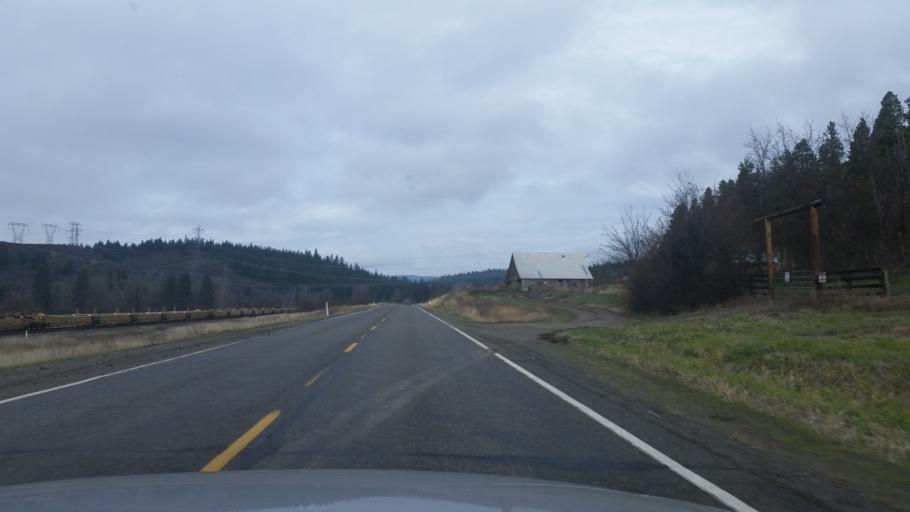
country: US
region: Washington
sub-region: Kittitas County
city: Cle Elum
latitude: 47.1490
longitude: -120.8020
